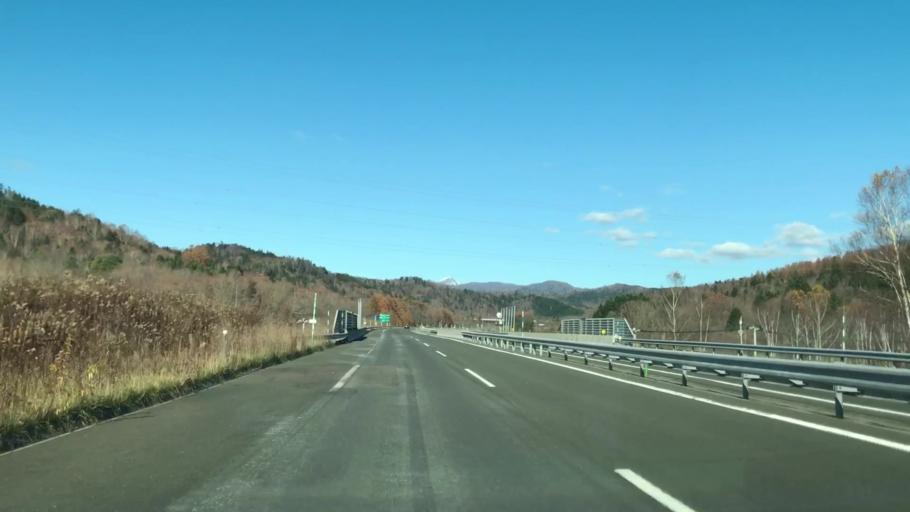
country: JP
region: Hokkaido
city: Shimo-furano
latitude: 42.9275
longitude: 142.2038
